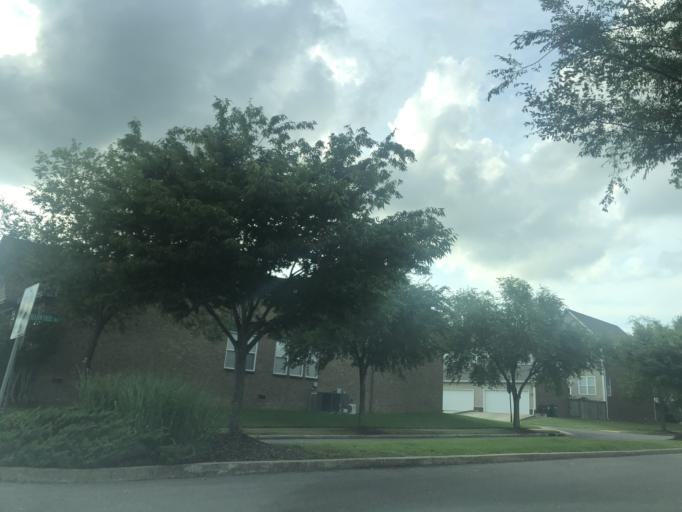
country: US
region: Tennessee
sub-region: Davidson County
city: Lakewood
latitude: 36.1682
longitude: -86.6171
